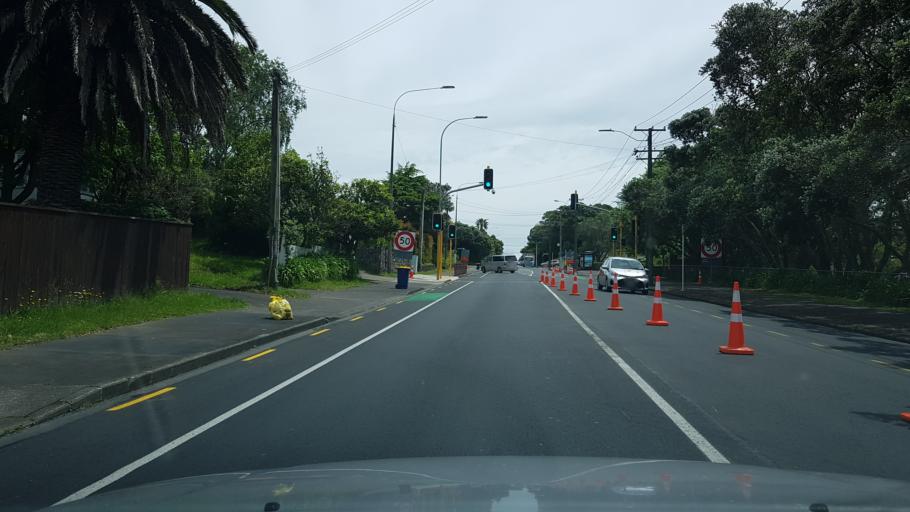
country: NZ
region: Auckland
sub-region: Auckland
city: North Shore
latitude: -36.8019
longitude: 174.7871
